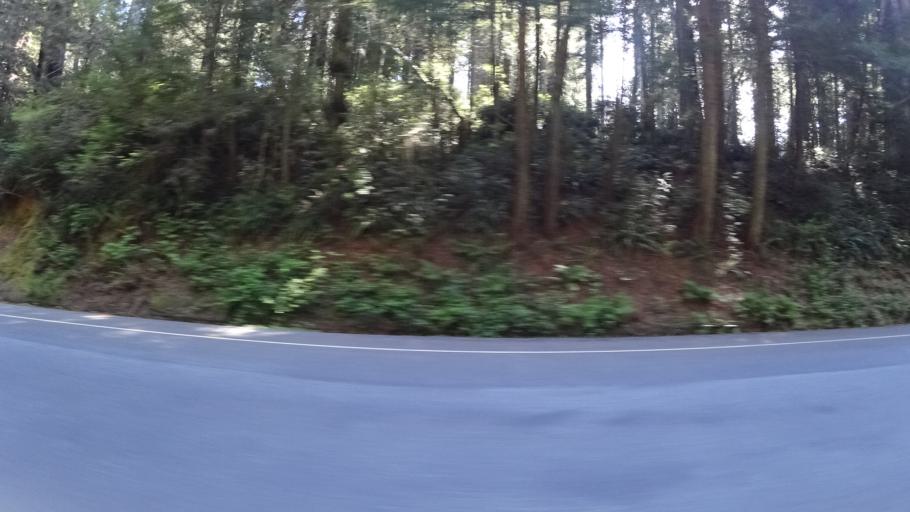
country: US
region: California
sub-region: Del Norte County
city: Bertsch-Oceanview
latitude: 41.6521
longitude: -124.1155
